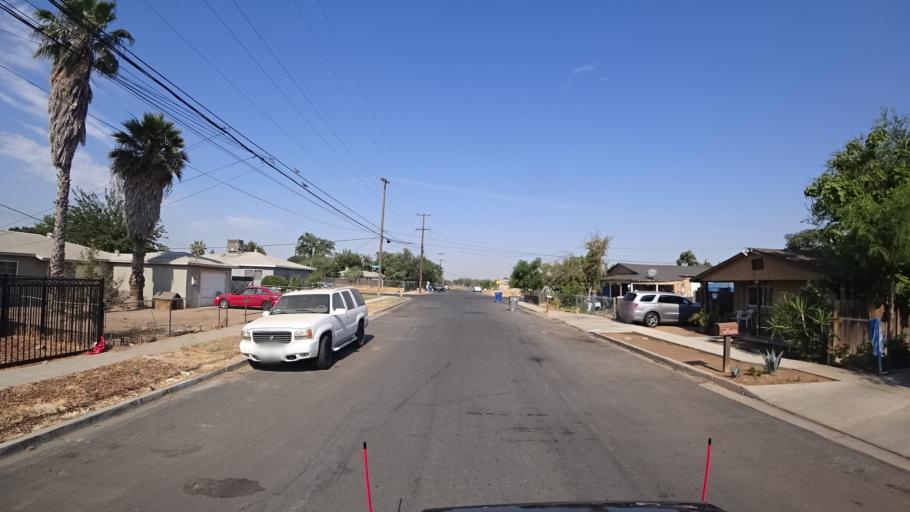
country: US
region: California
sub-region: Fresno County
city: West Park
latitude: 36.7195
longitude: -119.8150
